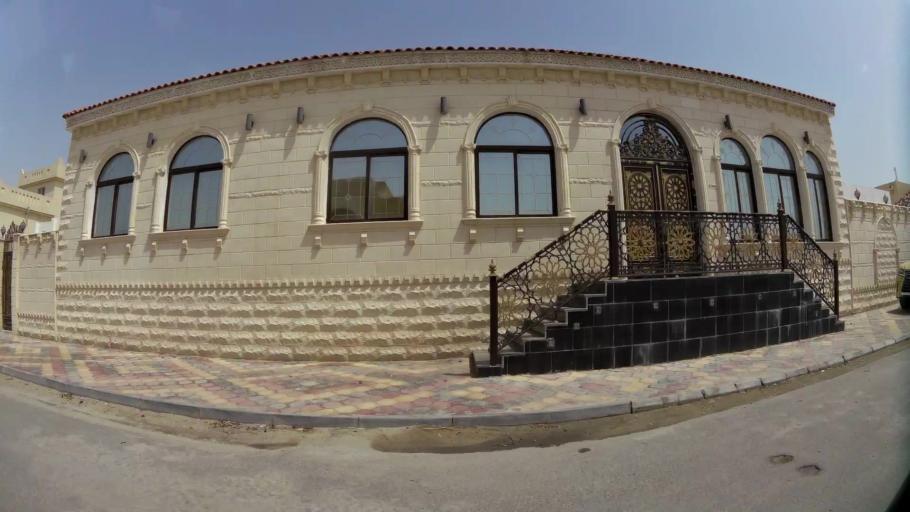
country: QA
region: Baladiyat ar Rayyan
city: Ar Rayyan
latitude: 25.2292
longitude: 51.4146
